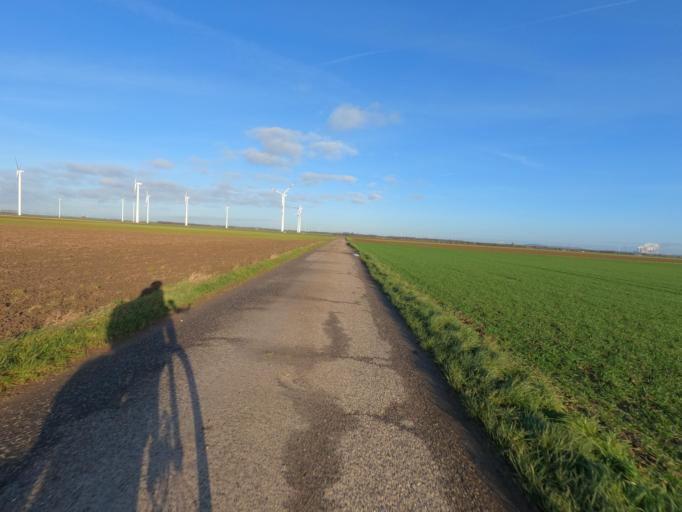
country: DE
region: North Rhine-Westphalia
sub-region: Regierungsbezirk Koln
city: Elsdorf
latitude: 50.9664
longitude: 6.5008
